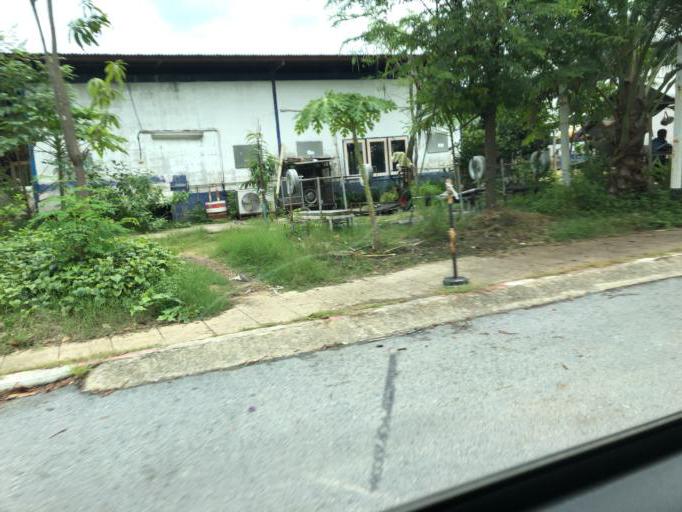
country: TH
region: Bangkok
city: Don Mueang
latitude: 13.9328
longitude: 100.6117
